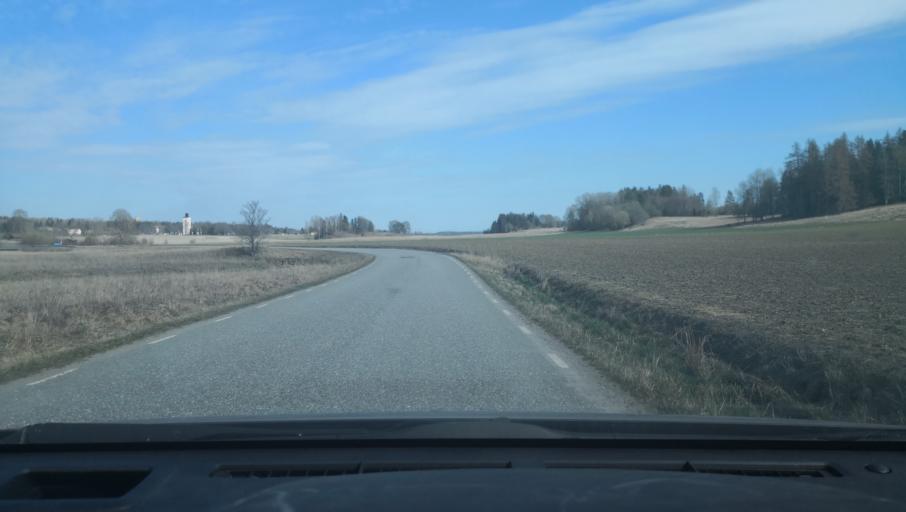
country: SE
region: Uppsala
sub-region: Enkopings Kommun
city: Irsta
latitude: 59.7712
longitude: 16.8790
